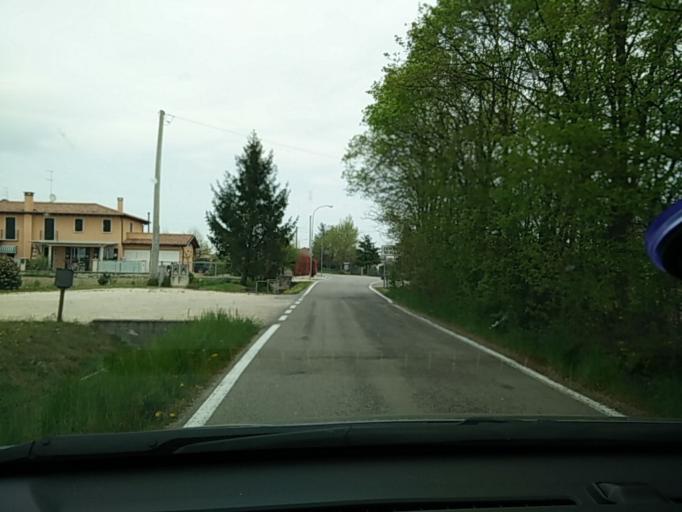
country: IT
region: Veneto
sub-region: Provincia di Treviso
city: Zenson di Piave
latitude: 45.6678
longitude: 12.4886
